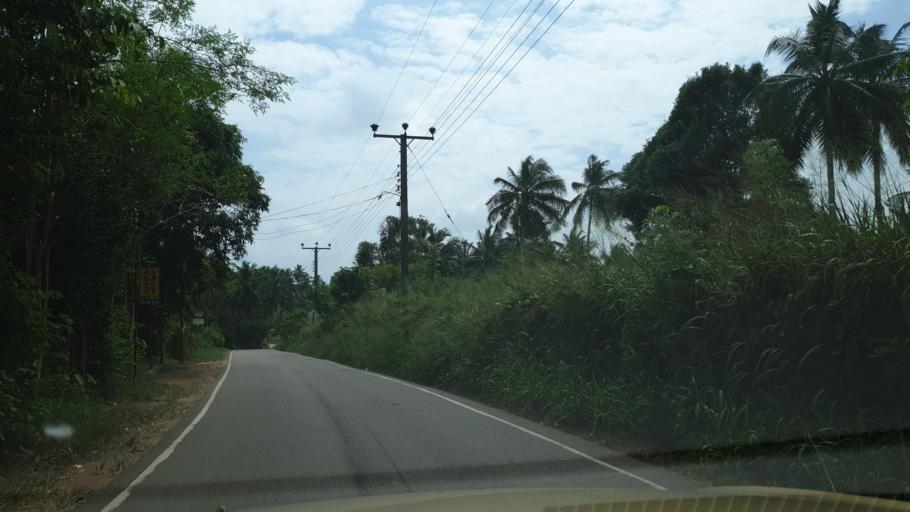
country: LK
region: North Western
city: Kuliyapitiya
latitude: 7.3492
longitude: 79.9787
